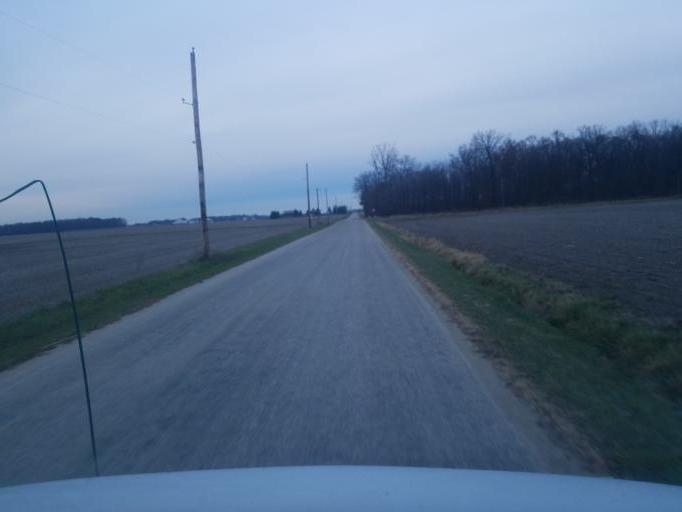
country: US
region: Indiana
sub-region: Adams County
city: Decatur
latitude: 40.7739
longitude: -84.8799
